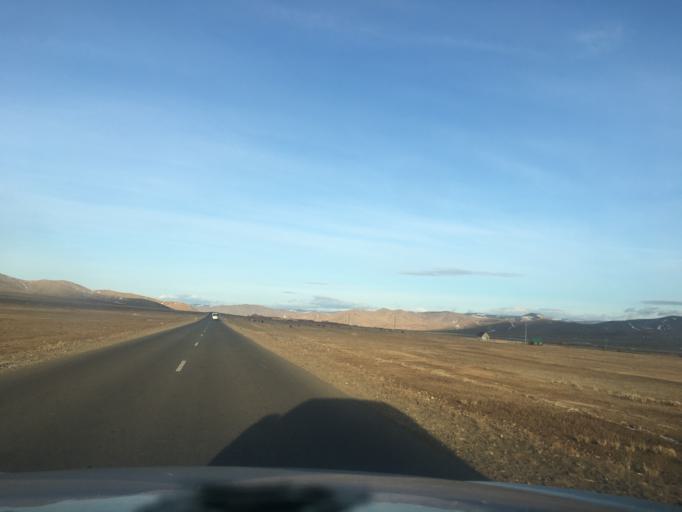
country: MN
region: Central Aimak
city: Mandal
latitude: 48.0952
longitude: 106.6108
